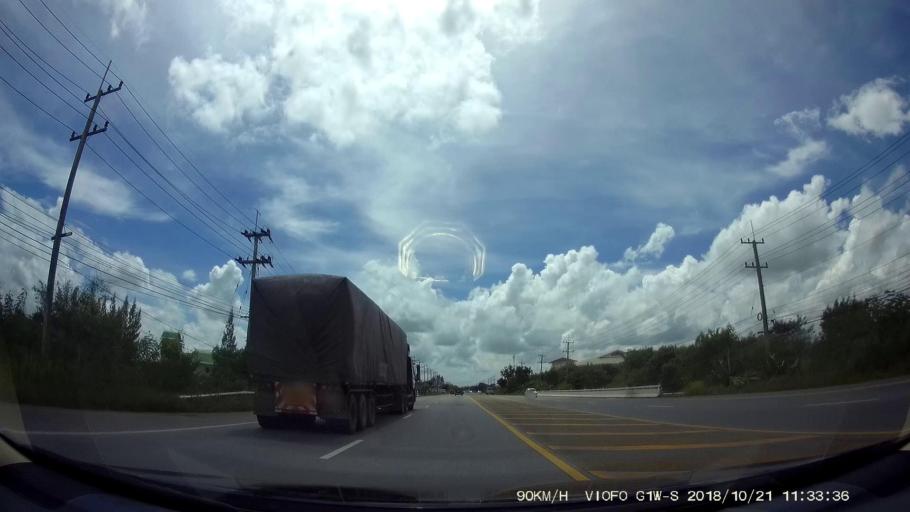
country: TH
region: Chaiyaphum
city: Chaiyaphum
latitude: 15.7434
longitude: 102.0243
